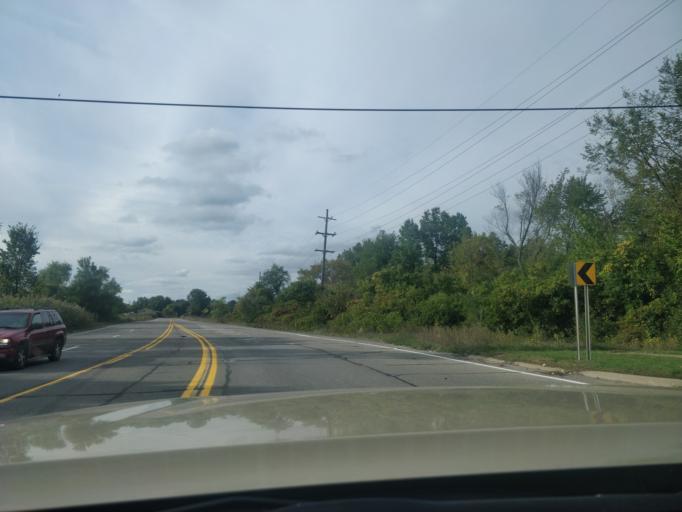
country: US
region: Michigan
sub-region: Wayne County
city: Romulus
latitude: 42.2230
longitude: -83.4408
